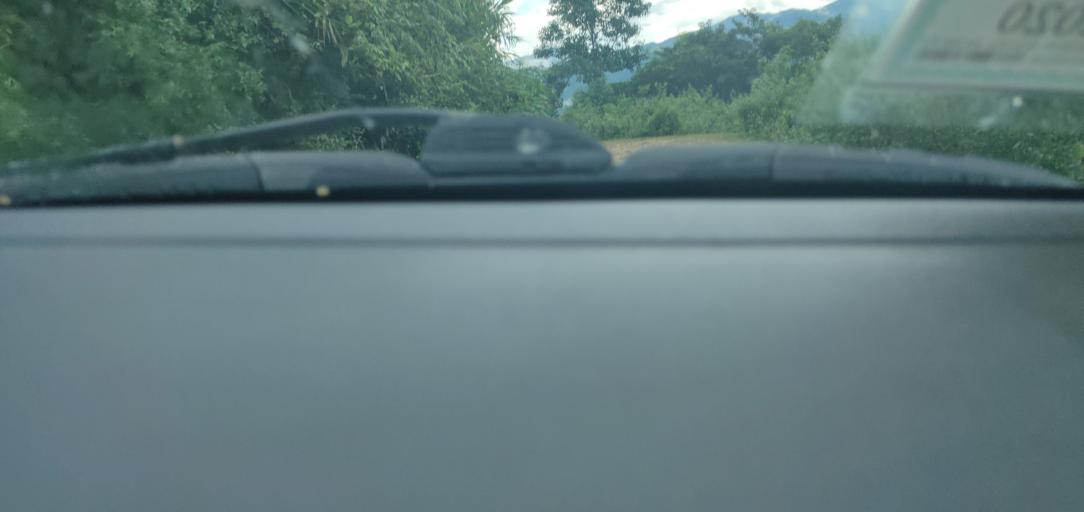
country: LA
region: Phongsali
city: Phongsali
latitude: 21.4435
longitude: 102.3165
